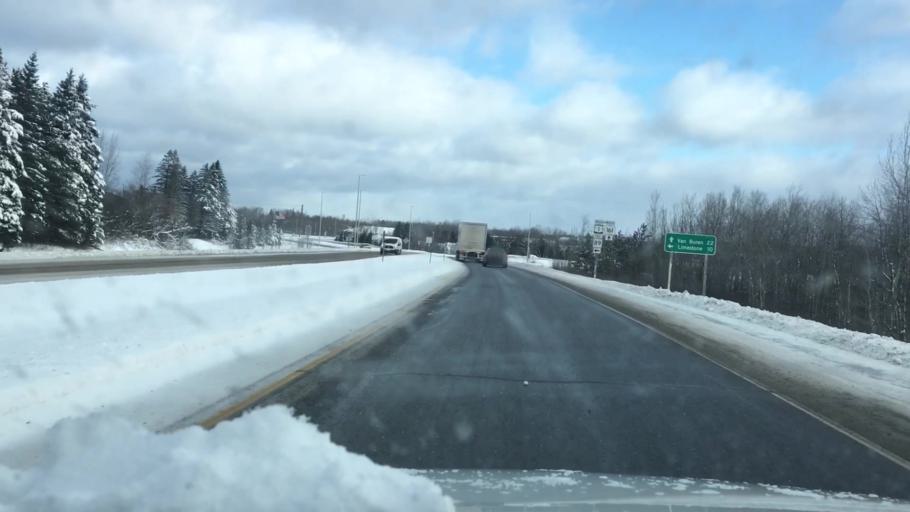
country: US
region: Maine
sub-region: Aroostook County
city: Caribou
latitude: 46.8659
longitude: -67.9994
